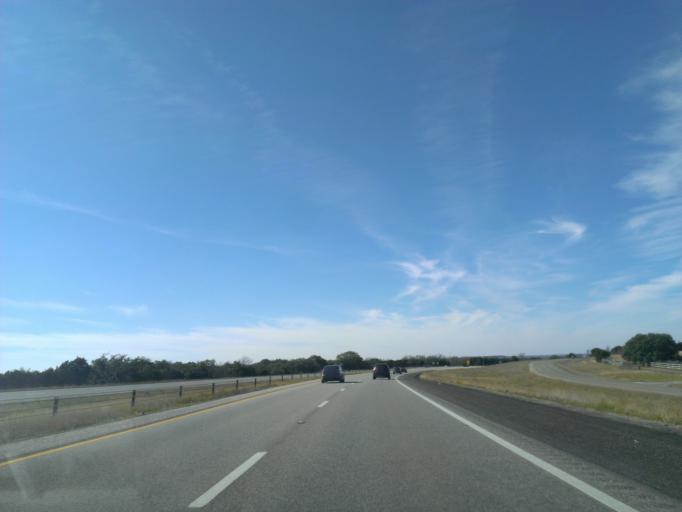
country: US
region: Texas
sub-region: Bell County
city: Nolanville
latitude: 31.0553
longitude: -97.5520
